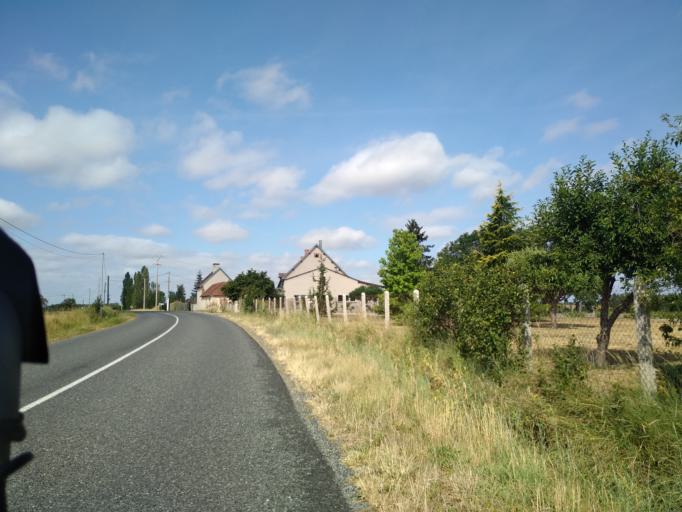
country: FR
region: Auvergne
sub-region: Departement de l'Allier
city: Saint-Pourcain-sur-Sioule
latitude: 46.2885
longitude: 3.2519
